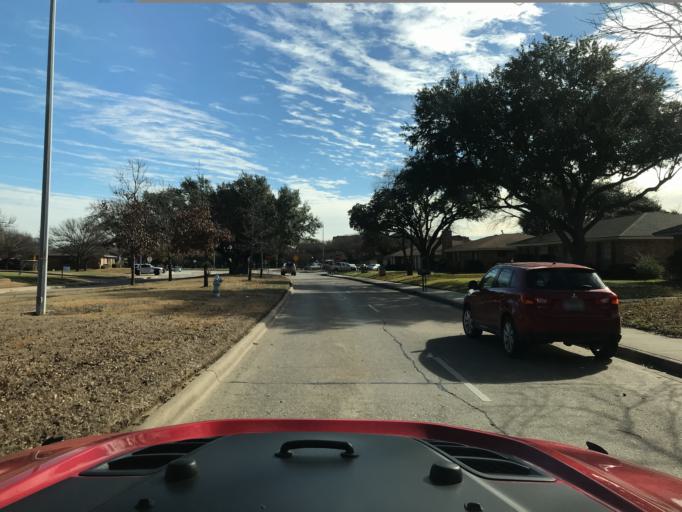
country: US
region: Texas
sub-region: Denton County
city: Lewisville
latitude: 33.0476
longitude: -97.0276
